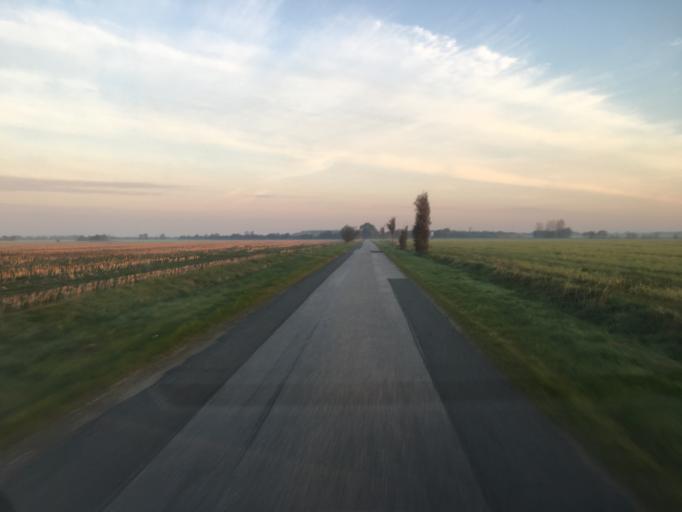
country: DK
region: South Denmark
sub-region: Tonder Kommune
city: Logumkloster
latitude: 55.0442
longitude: 9.0265
